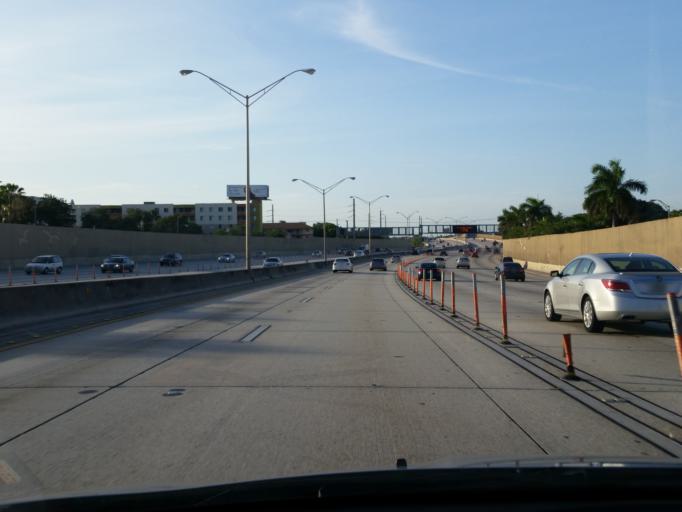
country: US
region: Florida
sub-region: Miami-Dade County
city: Allapattah
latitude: 25.8261
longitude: -80.2066
